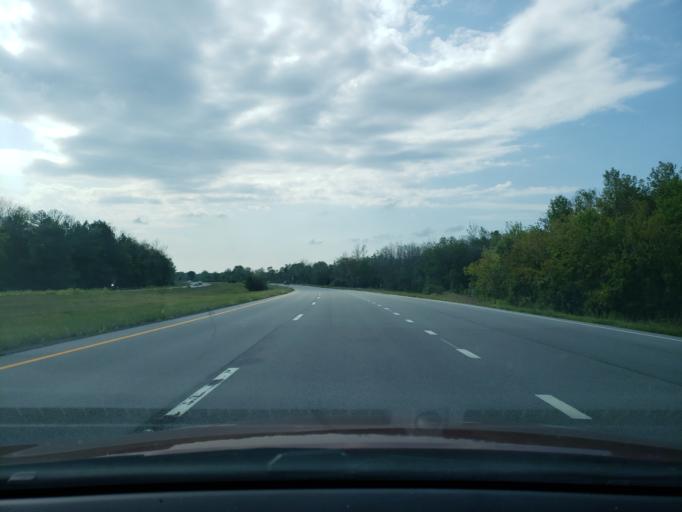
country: US
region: New York
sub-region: Monroe County
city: Greece
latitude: 43.2722
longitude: -77.6689
